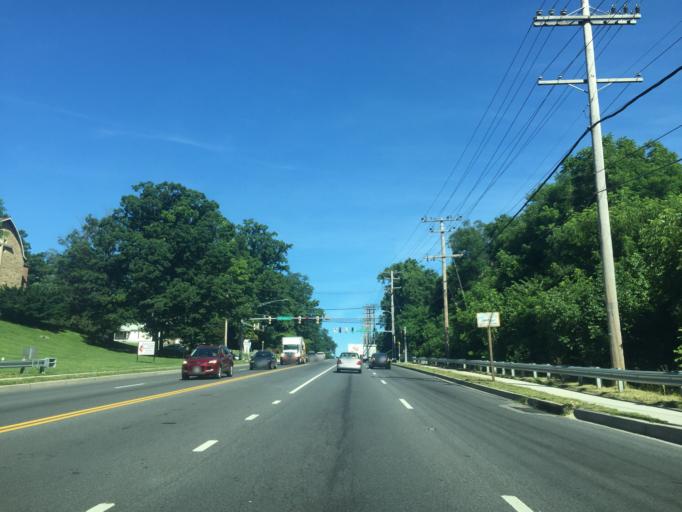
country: US
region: Maryland
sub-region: Baltimore County
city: Lochearn
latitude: 39.3424
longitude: -76.7268
